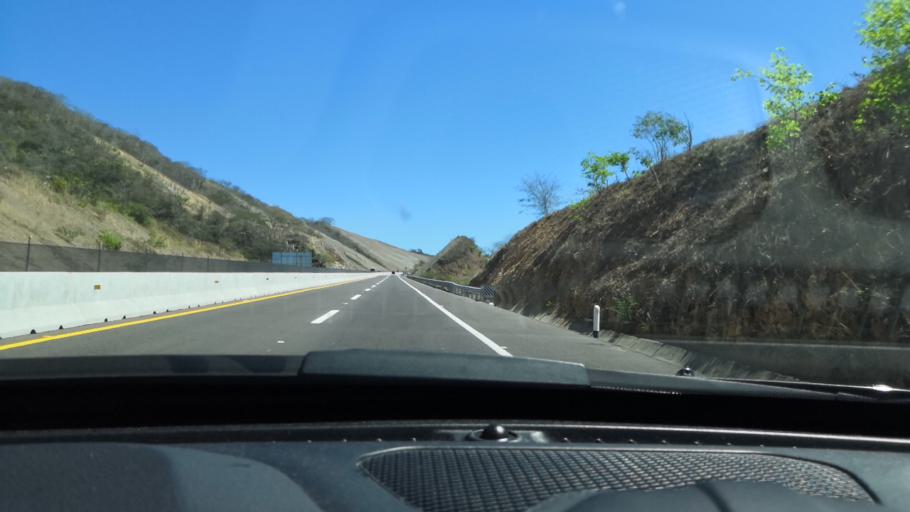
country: MX
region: Nayarit
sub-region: Compostela
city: Juan Escutia (Borbollon)
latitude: 21.1267
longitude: -104.8955
